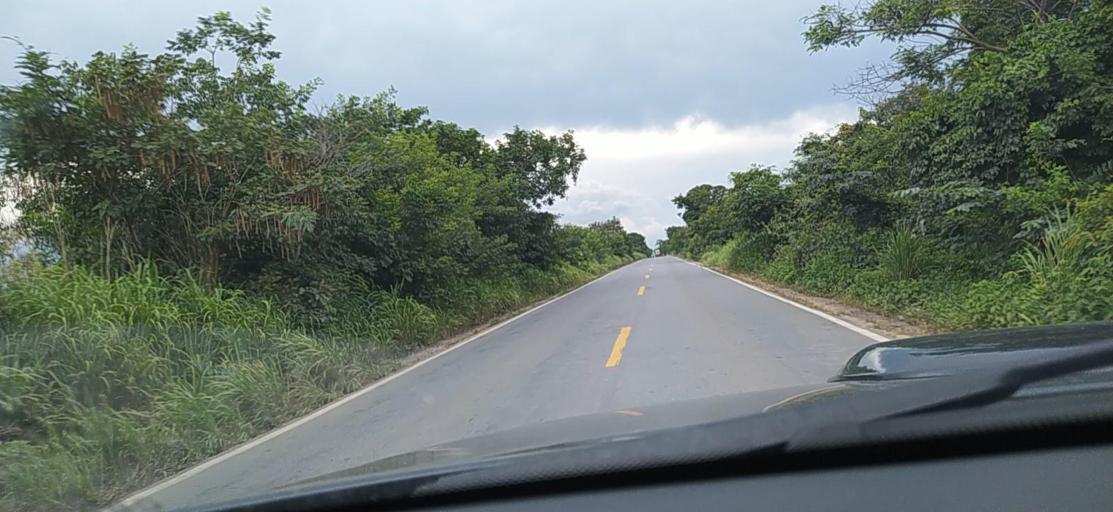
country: BR
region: Minas Gerais
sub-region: Francisco Sa
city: Francisco Sa
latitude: -16.2505
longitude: -43.6317
